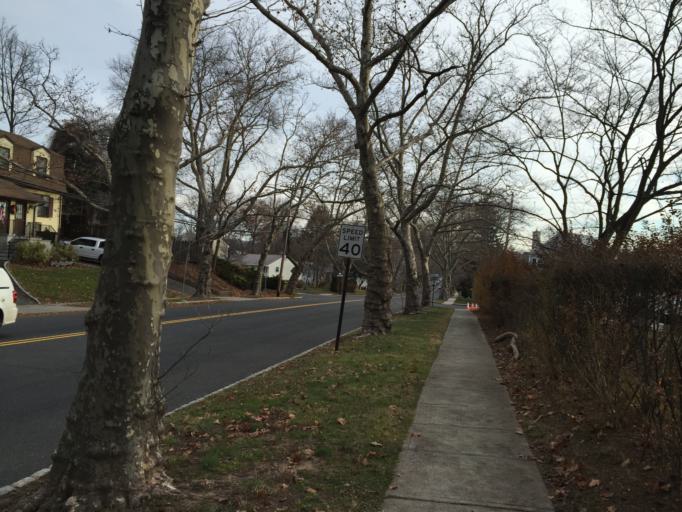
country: US
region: New Jersey
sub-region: Union County
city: Springfield
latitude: 40.7169
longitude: -74.3400
